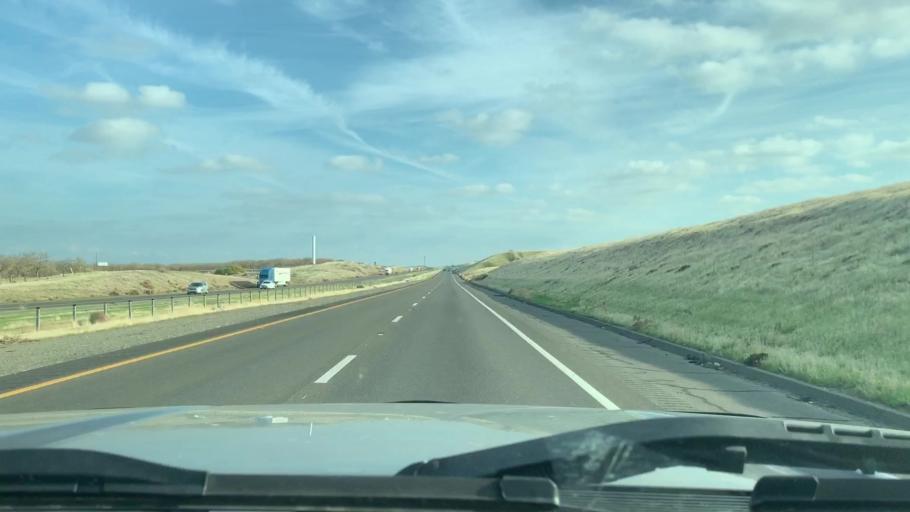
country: US
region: California
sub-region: Kings County
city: Kettleman City
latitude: 36.0387
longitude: -120.0379
